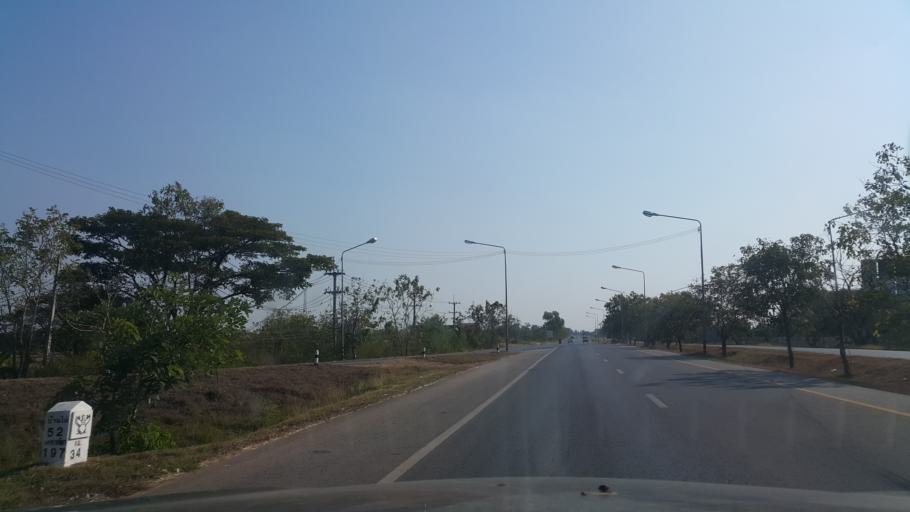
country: TH
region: Khon Kaen
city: Khon Kaen
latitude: 16.4345
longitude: 102.9178
